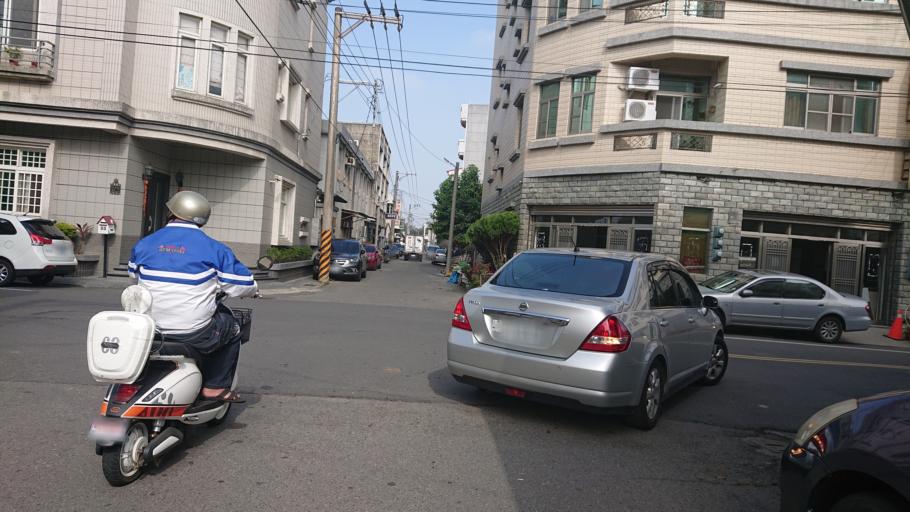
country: TW
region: Taiwan
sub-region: Chiayi
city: Taibao
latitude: 23.4683
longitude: 120.2438
